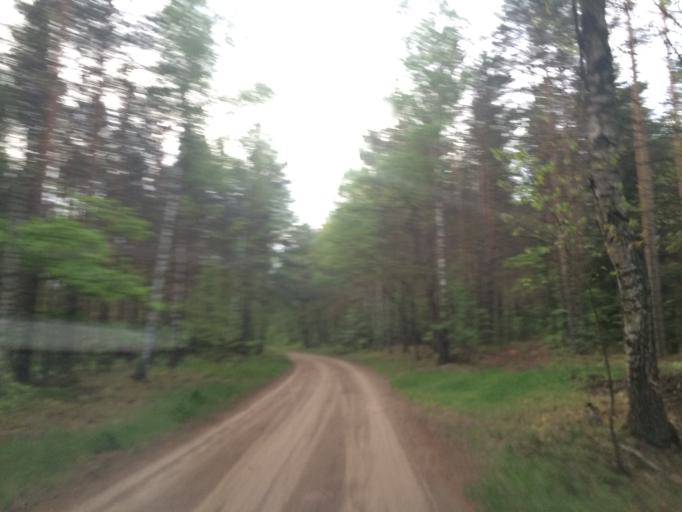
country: PL
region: Warmian-Masurian Voivodeship
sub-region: Powiat nowomiejski
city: Kurzetnik
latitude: 53.3577
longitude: 19.5183
